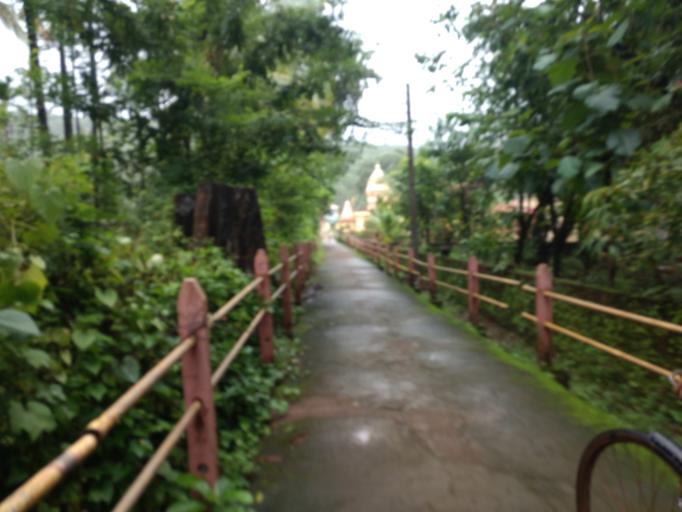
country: IN
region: Maharashtra
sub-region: Ratnagiri
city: Guhagar
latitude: 17.4948
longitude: 73.1867
